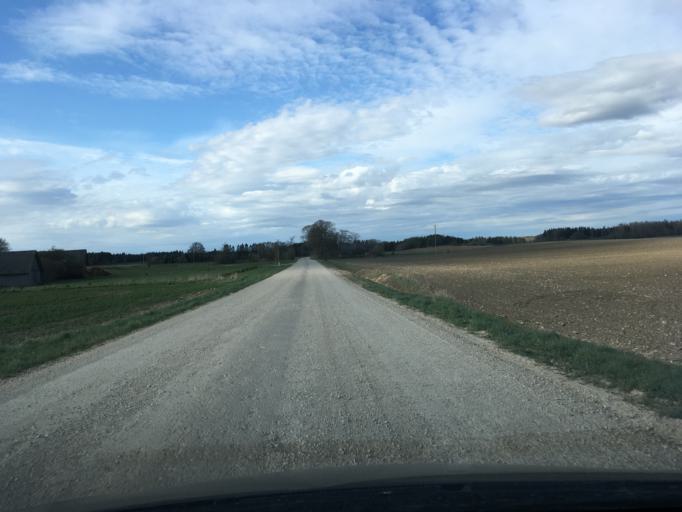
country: EE
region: Raplamaa
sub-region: Maerjamaa vald
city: Marjamaa
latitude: 58.9336
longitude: 24.3079
